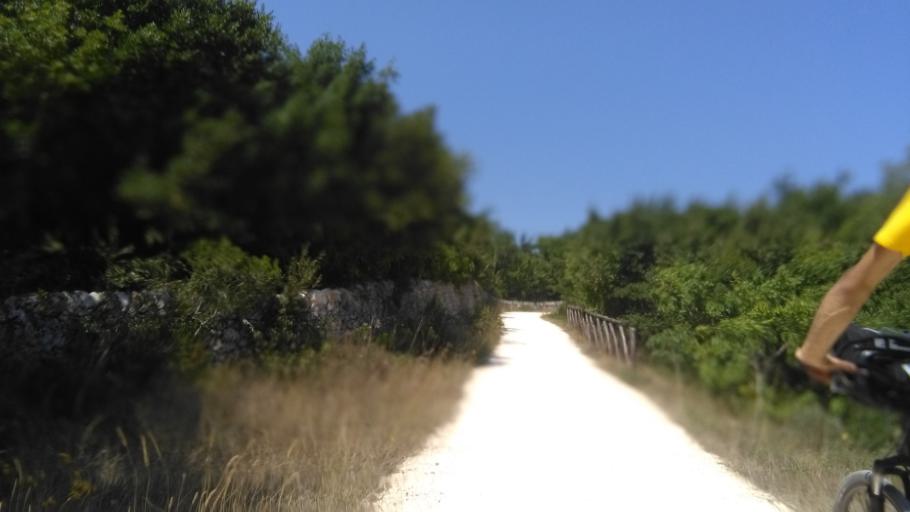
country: IT
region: Apulia
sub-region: Provincia di Brindisi
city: Cisternino
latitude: 40.6851
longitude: 17.4313
